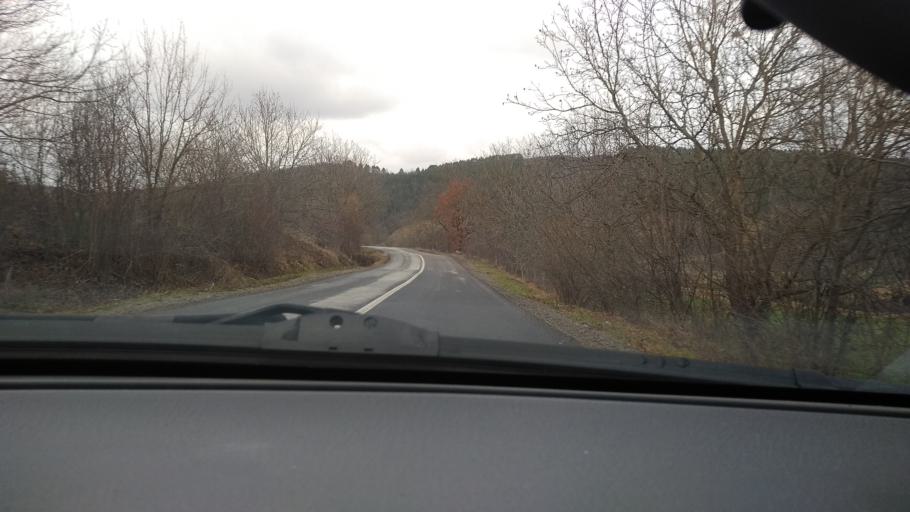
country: RO
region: Mures
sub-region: Comuna Pasareni
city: Pasareni
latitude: 46.5350
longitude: 24.6998
